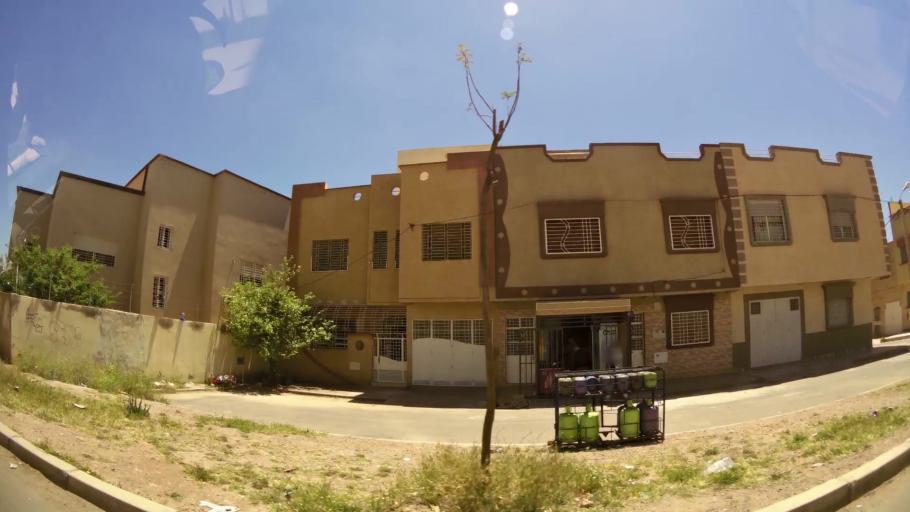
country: MA
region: Oriental
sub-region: Oujda-Angad
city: Oujda
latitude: 34.6645
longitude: -1.9213
